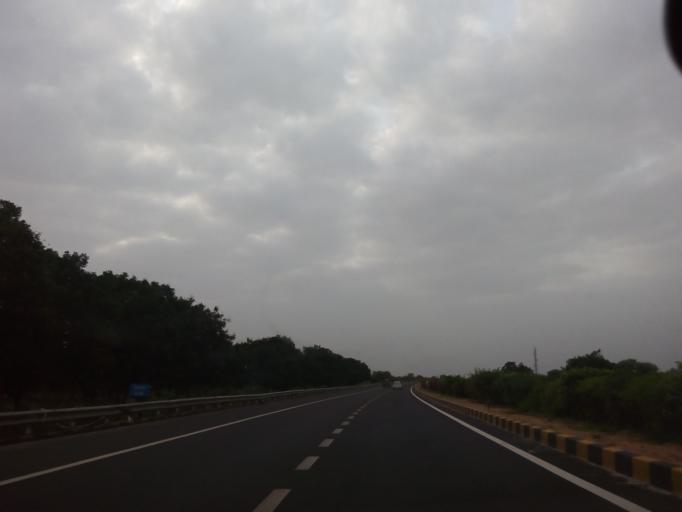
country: IN
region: Gujarat
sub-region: Kheda
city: Mahemdavad
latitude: 22.9201
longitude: 72.7541
